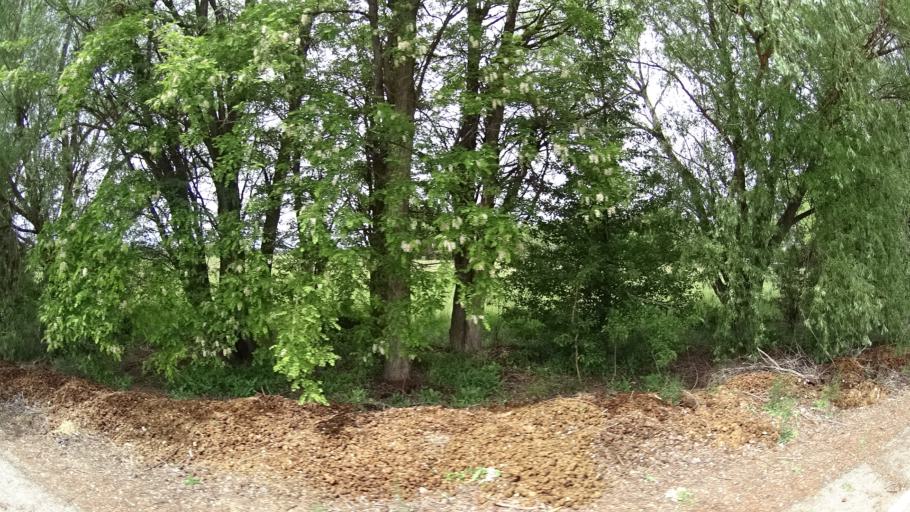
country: US
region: Idaho
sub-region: Ada County
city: Eagle
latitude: 43.7155
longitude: -116.4035
